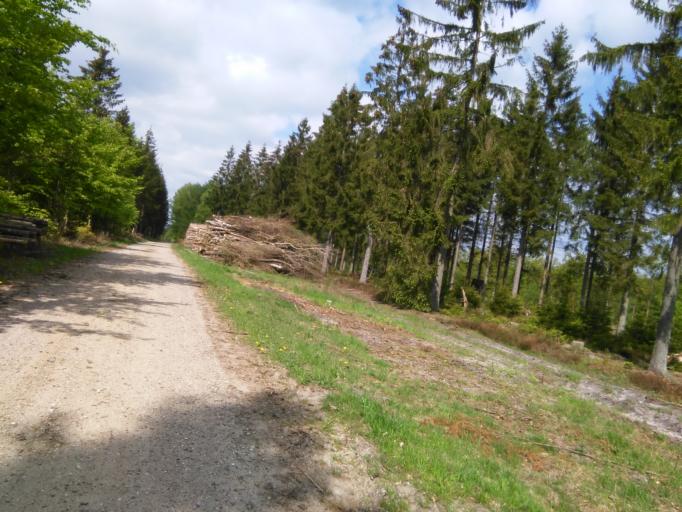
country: DK
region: Central Jutland
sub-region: Silkeborg Kommune
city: Svejbaek
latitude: 56.0573
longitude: 9.6556
